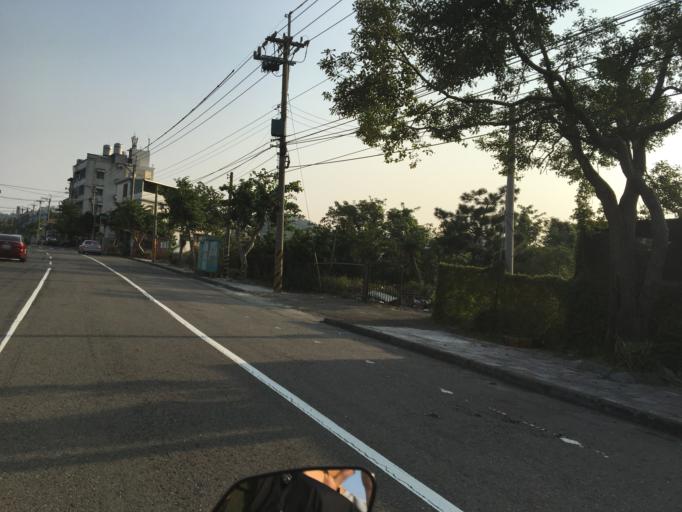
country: TW
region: Taiwan
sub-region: Hsinchu
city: Hsinchu
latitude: 24.7293
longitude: 120.9170
